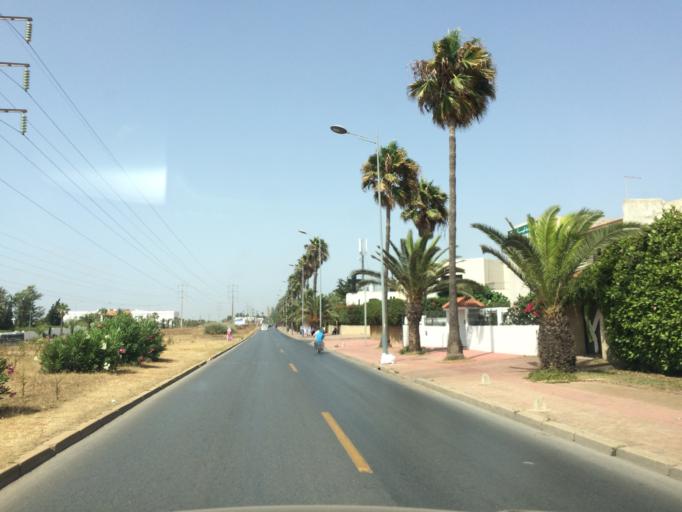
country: MA
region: Rabat-Sale-Zemmour-Zaer
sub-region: Skhirate-Temara
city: Temara
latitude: 33.9661
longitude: -6.8694
